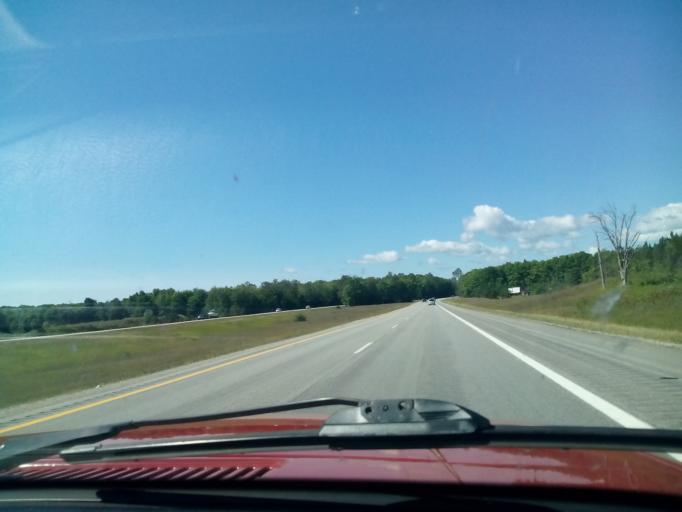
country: US
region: Michigan
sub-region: Cheboygan County
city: Indian River
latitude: 45.3204
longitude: -84.5985
